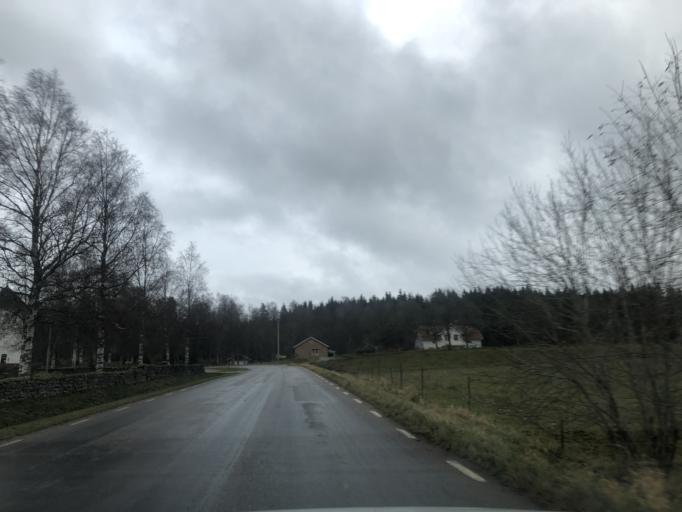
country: SE
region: Vaestra Goetaland
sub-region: Ulricehamns Kommun
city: Ulricehamn
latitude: 57.8997
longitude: 13.4756
